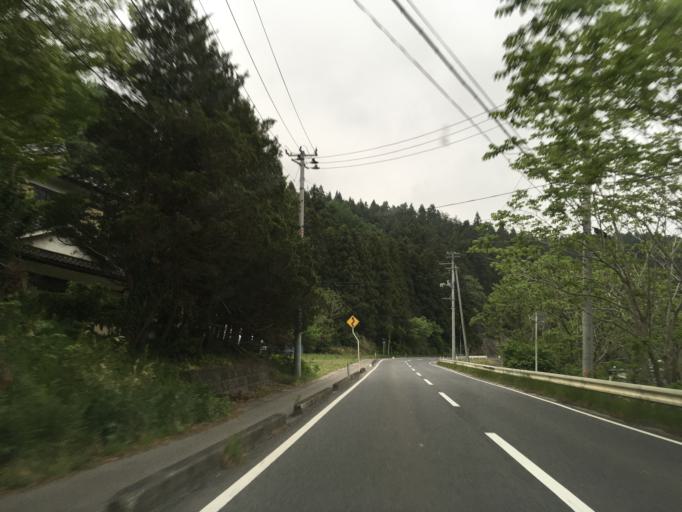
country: JP
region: Iwate
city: Ichinoseki
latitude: 38.7341
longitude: 141.3035
